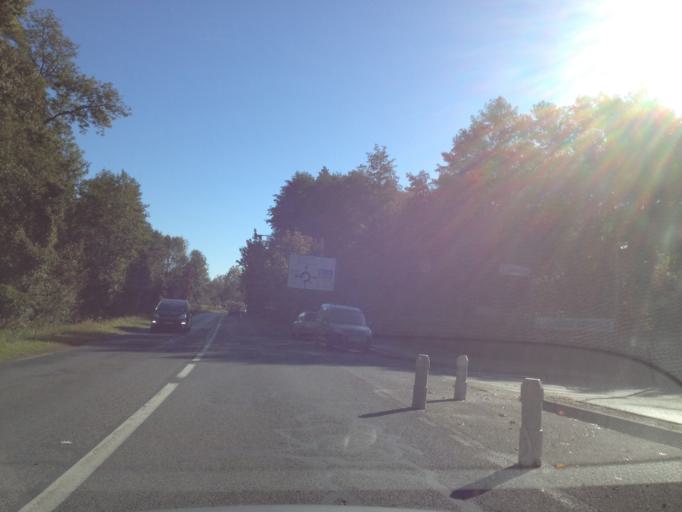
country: FR
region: Rhone-Alpes
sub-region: Departement de l'Isere
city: Morestel
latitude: 45.6734
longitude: 5.4664
